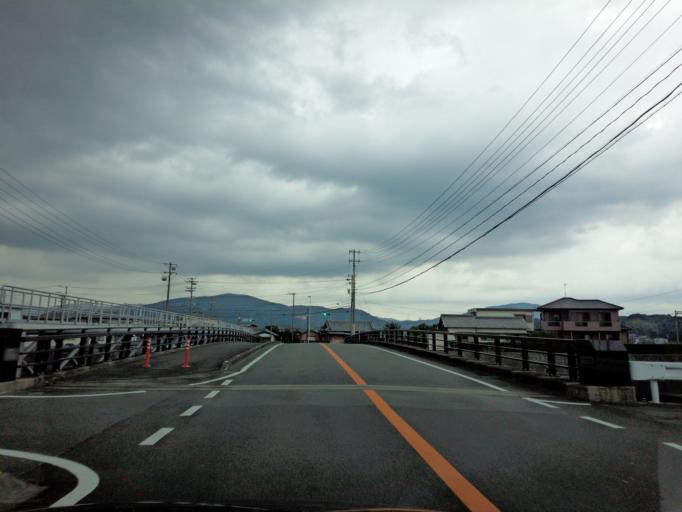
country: JP
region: Mie
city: Toba
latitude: 34.3635
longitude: 136.8109
